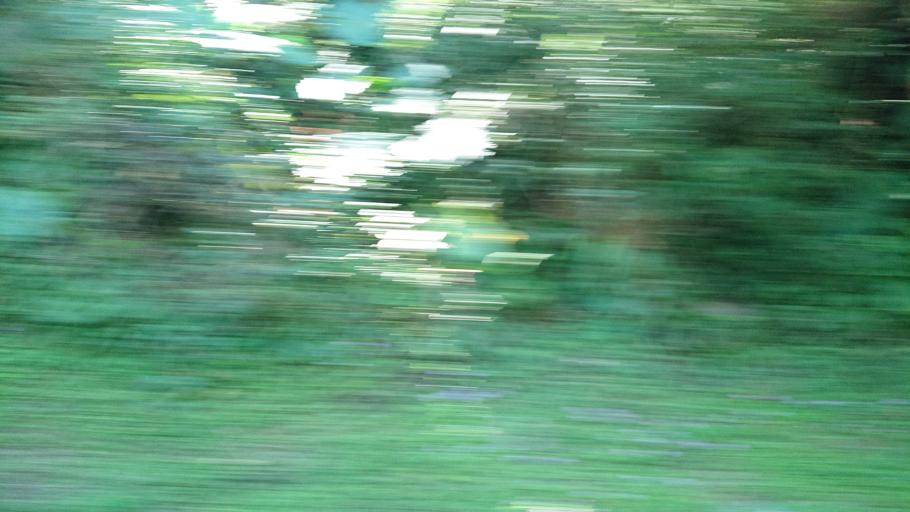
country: TW
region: Taiwan
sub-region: Yilan
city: Yilan
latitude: 24.5776
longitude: 121.4900
